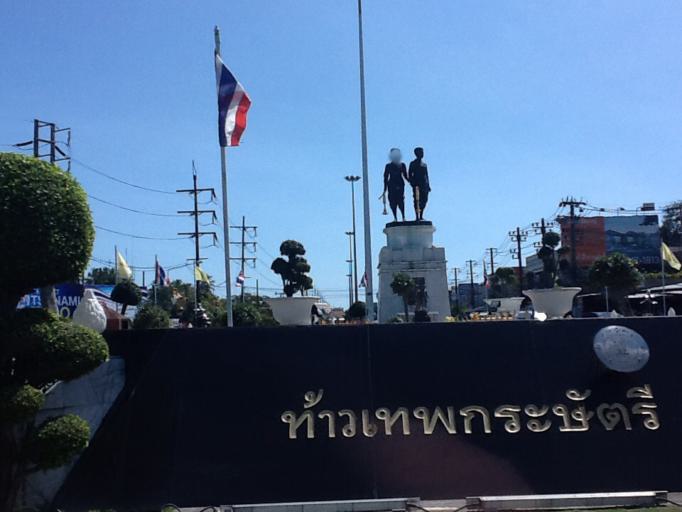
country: TH
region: Phuket
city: Ban Ko Kaeo
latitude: 7.9811
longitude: 98.3638
